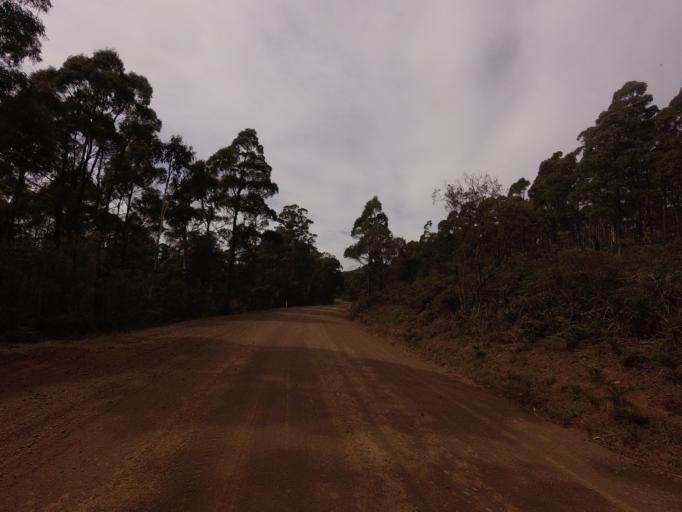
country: AU
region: Tasmania
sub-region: Sorell
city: Sorell
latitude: -42.4889
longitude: 147.6202
